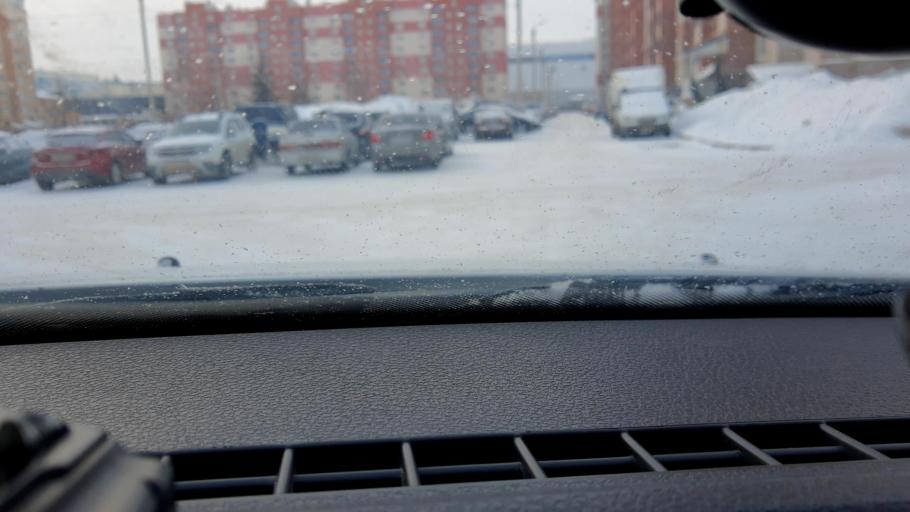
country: RU
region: Bashkortostan
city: Sterlitamak
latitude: 53.6339
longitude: 55.9005
